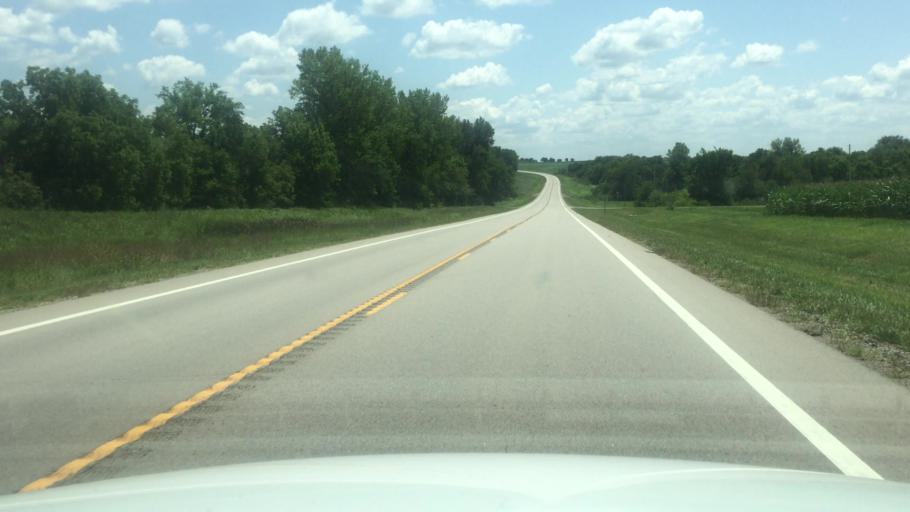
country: US
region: Kansas
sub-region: Brown County
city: Horton
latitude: 39.6254
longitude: -95.3505
